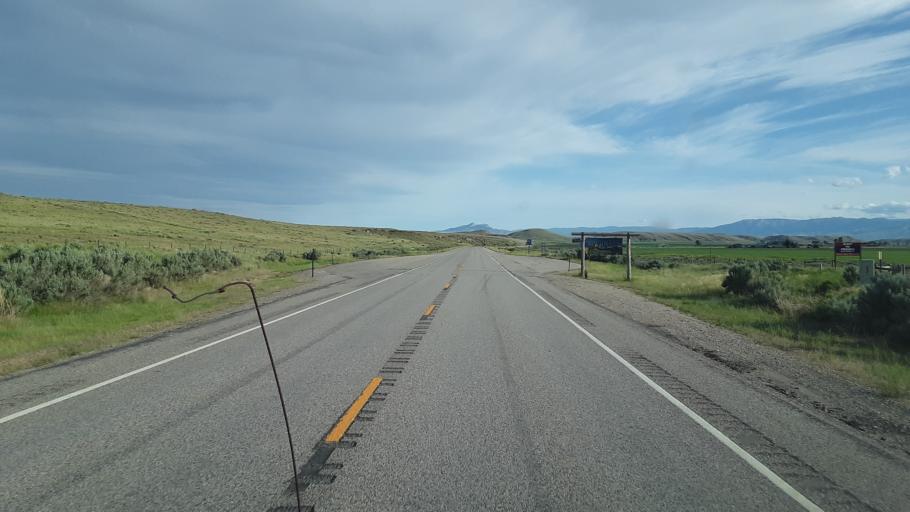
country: US
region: Montana
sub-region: Carbon County
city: Red Lodge
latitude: 45.0000
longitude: -109.0545
